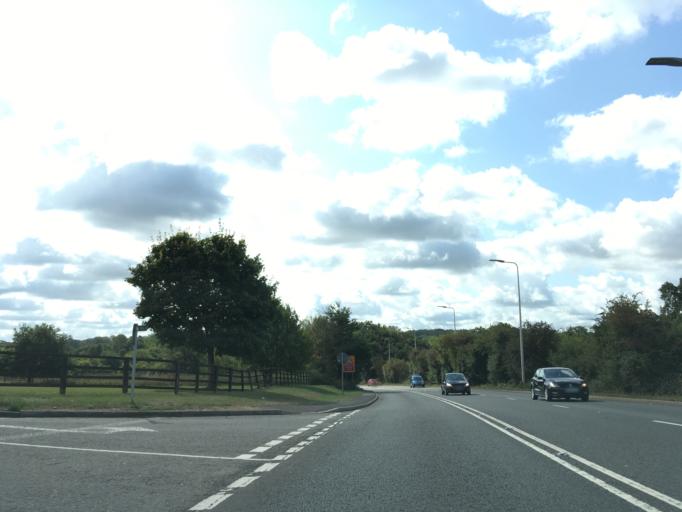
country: GB
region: England
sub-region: West Berkshire
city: Greenham
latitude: 51.3764
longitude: -1.3188
